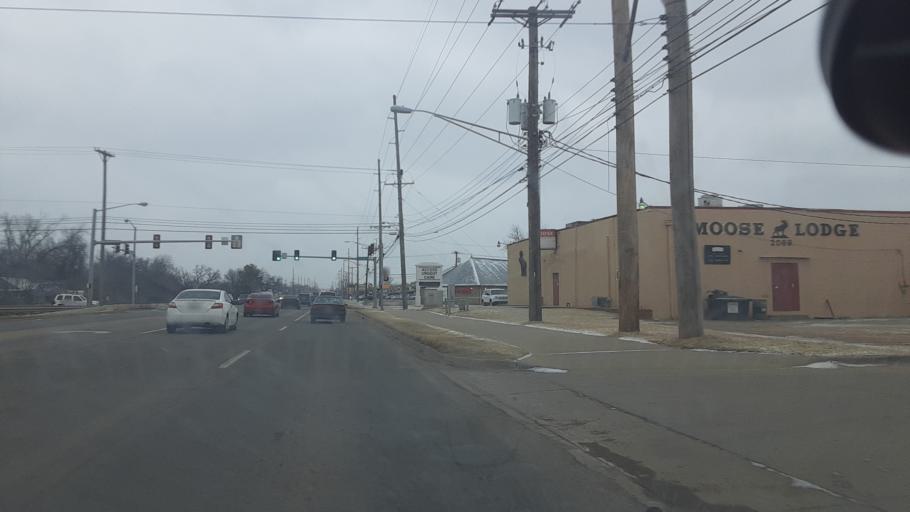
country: US
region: Oklahoma
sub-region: Payne County
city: Stillwater
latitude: 36.1183
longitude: -97.0513
